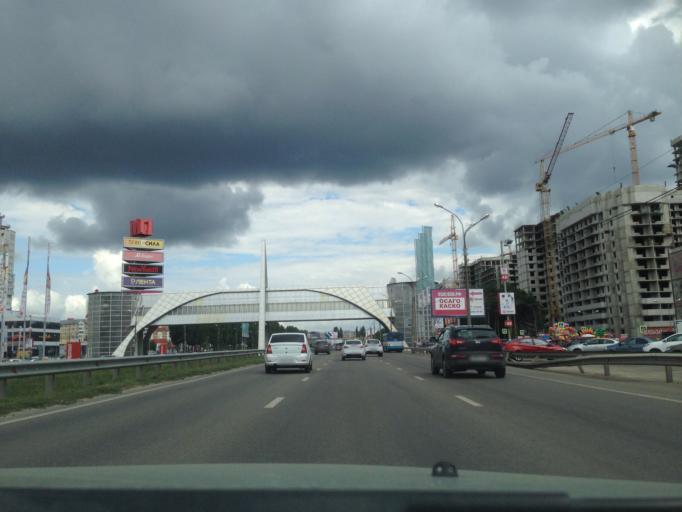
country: RU
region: Voronezj
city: Podgornoye
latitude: 51.7167
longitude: 39.1802
